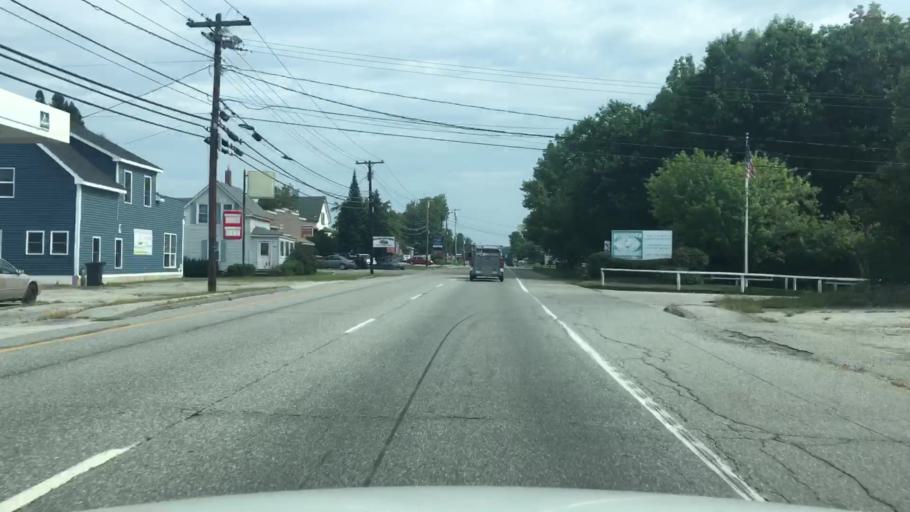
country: US
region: Maine
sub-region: Androscoggin County
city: Auburn
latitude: 44.0730
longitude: -70.2426
